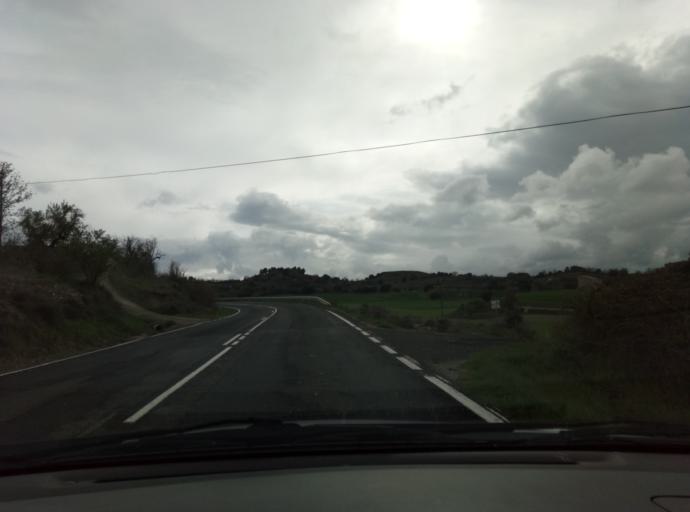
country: ES
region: Catalonia
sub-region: Provincia de Lleida
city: Cervera
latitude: 41.6234
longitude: 1.3390
